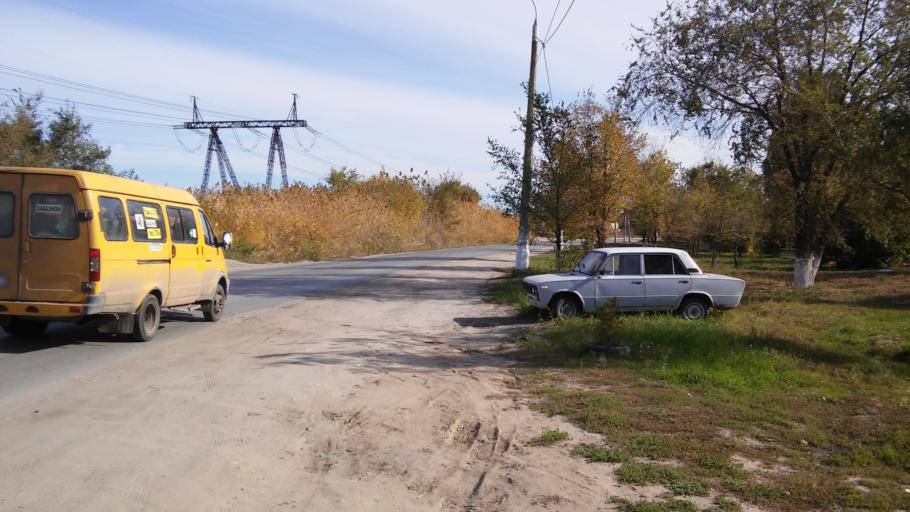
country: RU
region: Volgograd
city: Vodstroy
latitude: 48.8433
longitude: 44.6416
